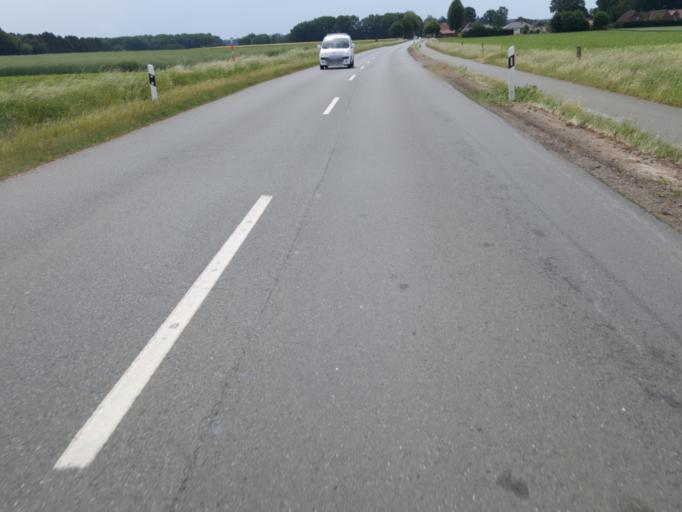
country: DE
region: Lower Saxony
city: Husum
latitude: 52.5851
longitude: 9.2491
